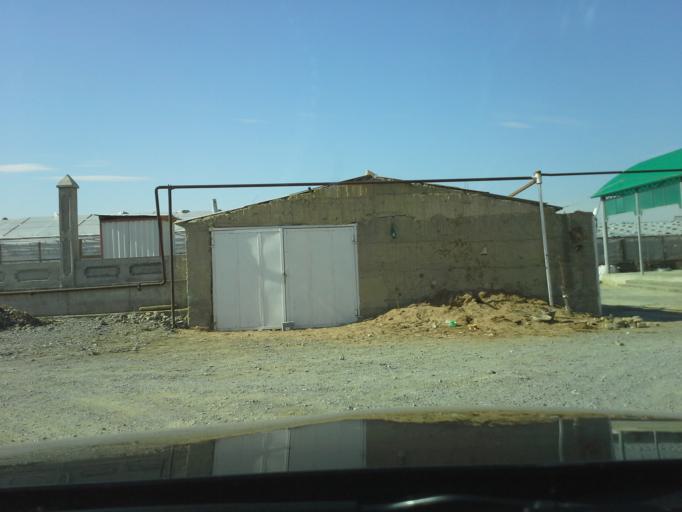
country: TM
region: Ahal
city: Abadan
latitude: 38.0850
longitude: 58.0174
